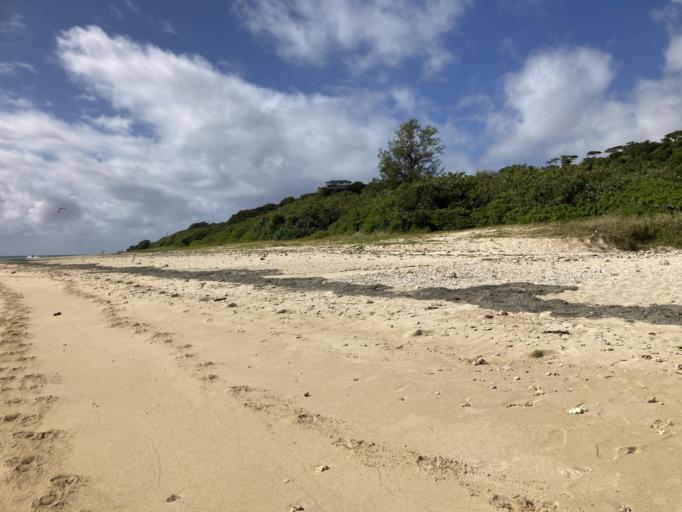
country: JP
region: Okinawa
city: Tomigusuku
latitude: 26.1391
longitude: 127.7962
